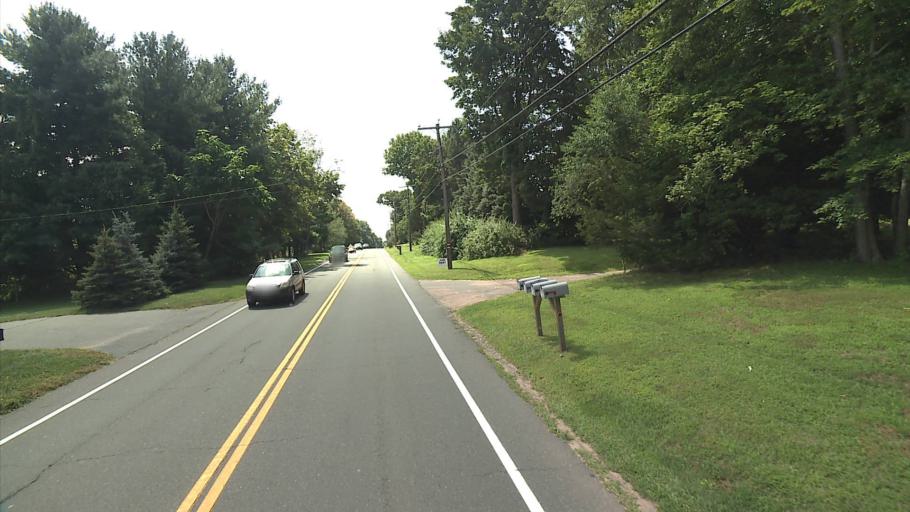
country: US
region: Connecticut
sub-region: Tolland County
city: Ellington
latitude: 41.8823
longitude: -72.4831
